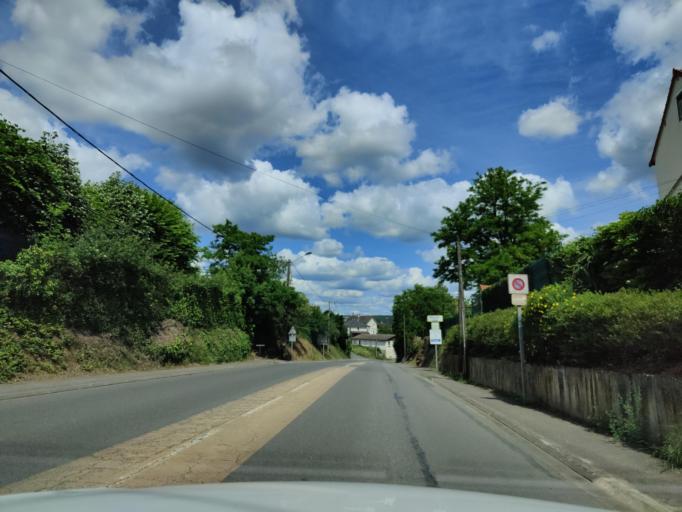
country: FR
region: Centre
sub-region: Departement du Cher
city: Saint-Amand-Montrond
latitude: 46.7132
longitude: 2.5059
